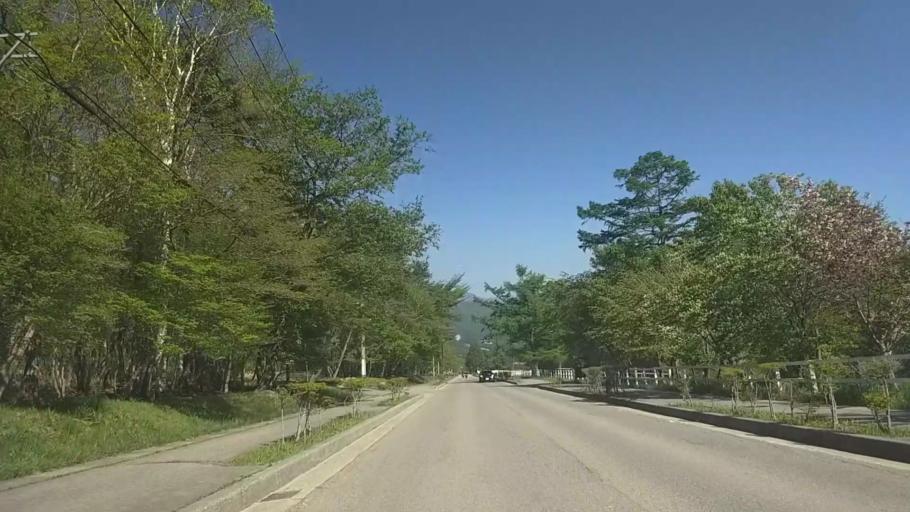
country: JP
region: Yamanashi
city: Nirasaki
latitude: 35.9240
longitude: 138.4234
